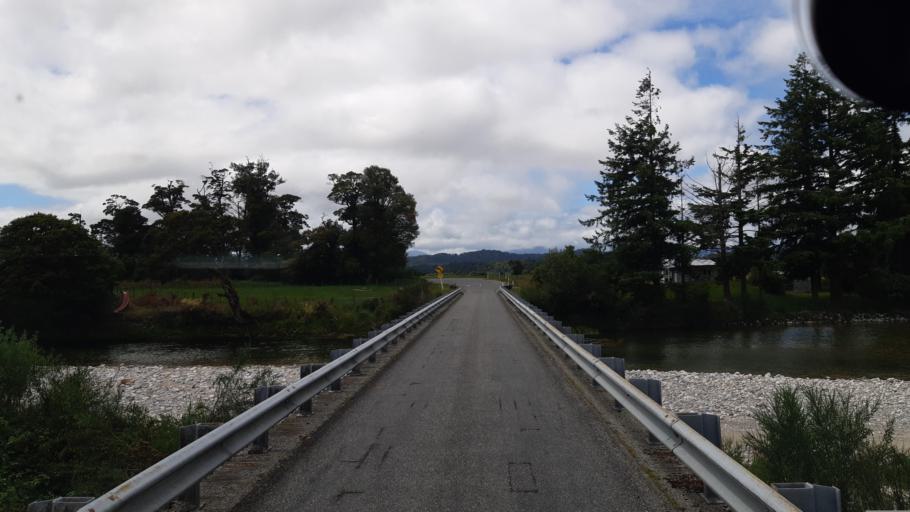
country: NZ
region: West Coast
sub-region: Grey District
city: Greymouth
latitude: -42.3174
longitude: 171.5383
